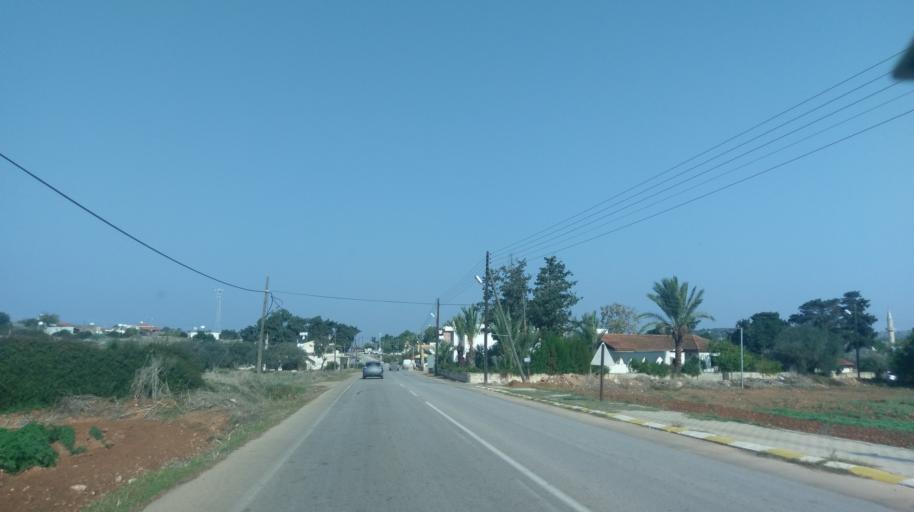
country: CY
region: Ammochostos
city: Leonarisso
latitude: 35.4999
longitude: 34.1603
